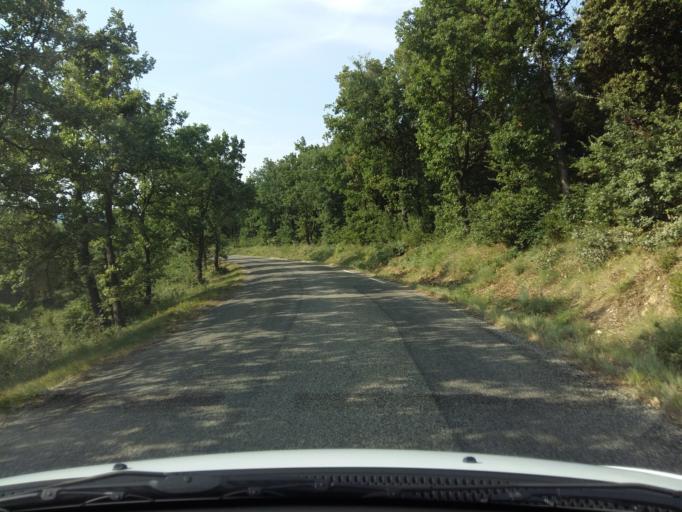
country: FR
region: Provence-Alpes-Cote d'Azur
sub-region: Departement du Vaucluse
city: Roussillon
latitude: 43.9404
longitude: 5.2709
